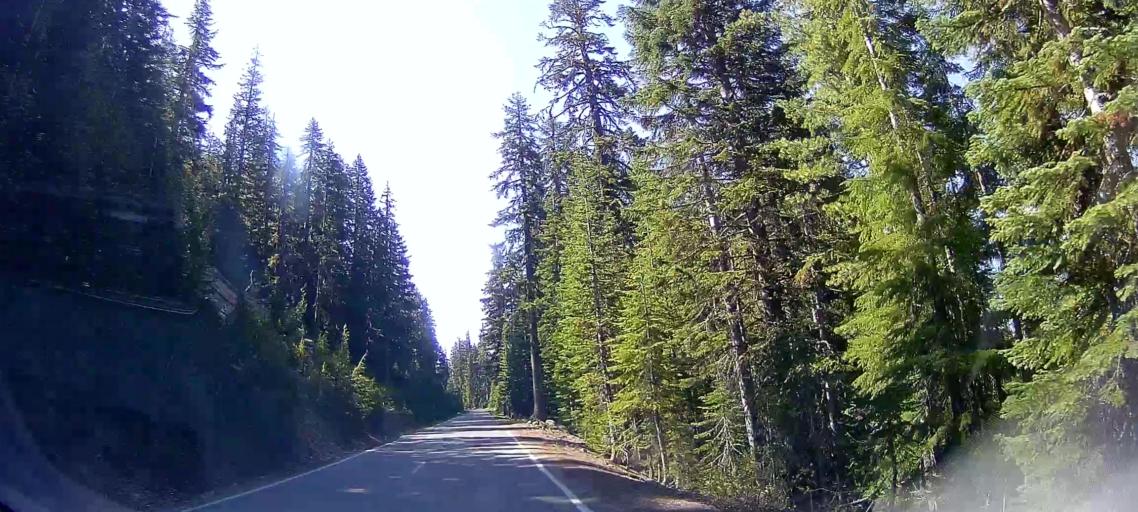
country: US
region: Oregon
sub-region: Jackson County
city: Shady Cove
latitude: 42.8847
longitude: -122.1298
